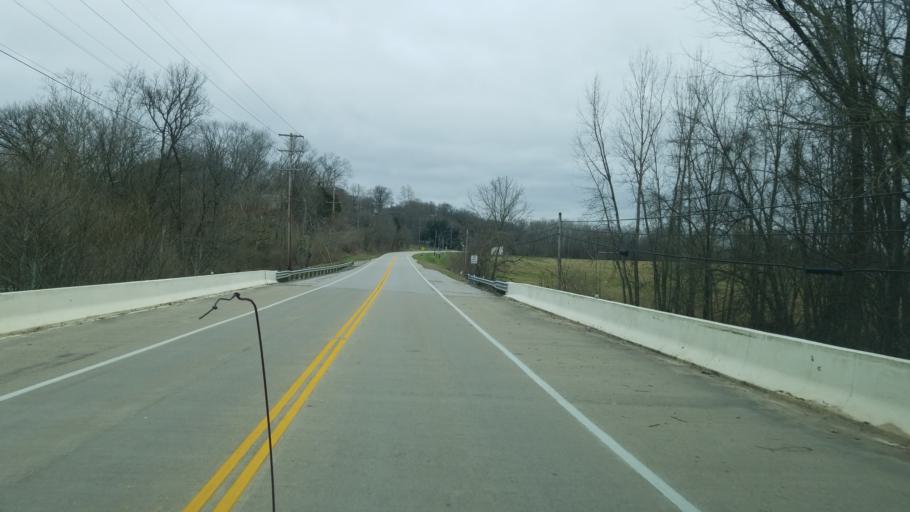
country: US
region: Ohio
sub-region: Clermont County
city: New Richmond
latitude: 38.9259
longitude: -84.2566
